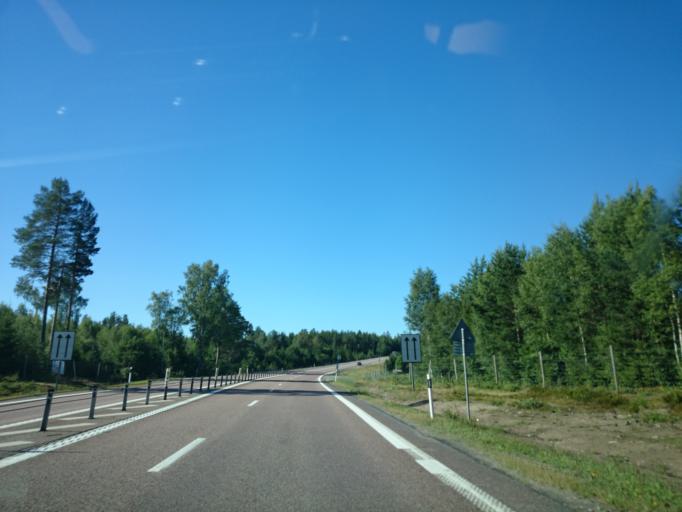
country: SE
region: Gaevleborg
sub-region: Hudiksvalls Kommun
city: Hudiksvall
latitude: 61.7983
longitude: 17.1703
